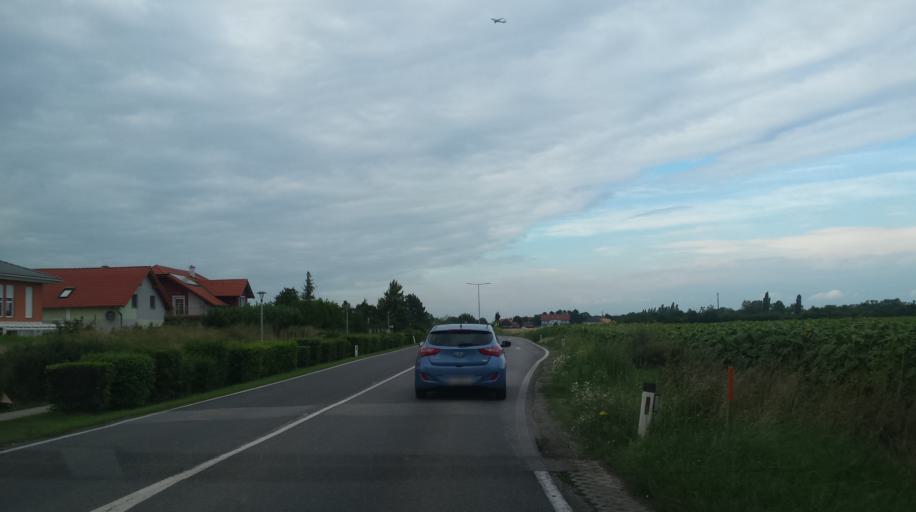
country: AT
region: Lower Austria
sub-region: Politischer Bezirk Wien-Umgebung
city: Zwolfaxing
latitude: 48.0996
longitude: 16.4558
